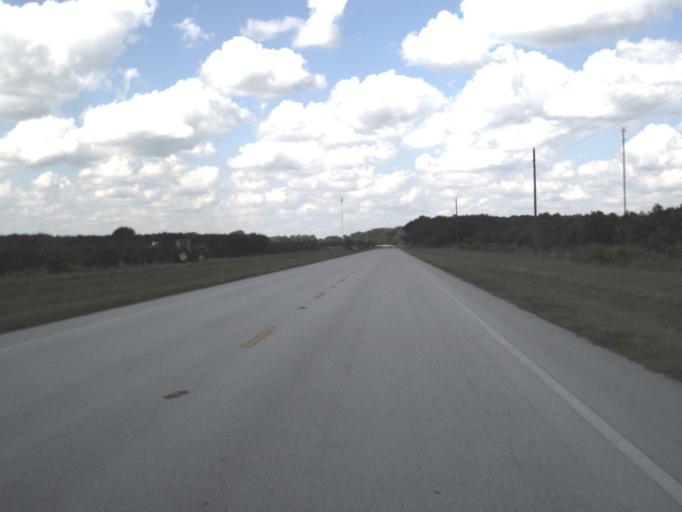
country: US
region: Florida
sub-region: Highlands County
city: Sebring
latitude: 27.4205
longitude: -81.5722
